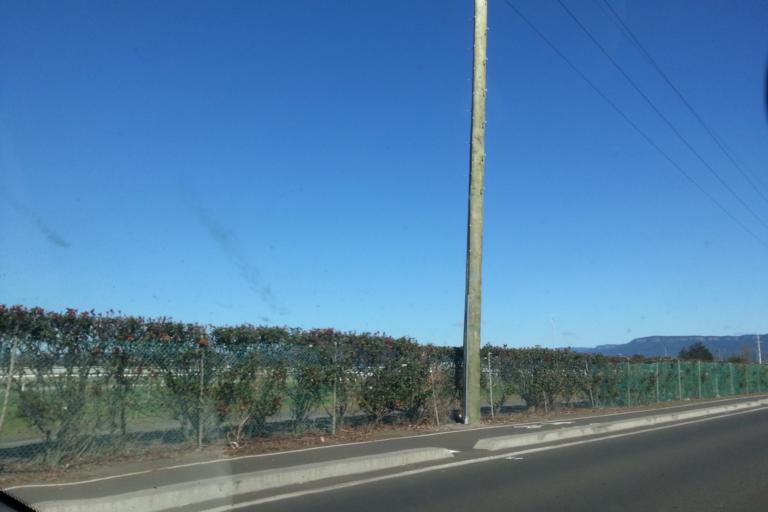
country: AU
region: New South Wales
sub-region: Wollongong
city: Berkeley
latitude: -34.4697
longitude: 150.8210
